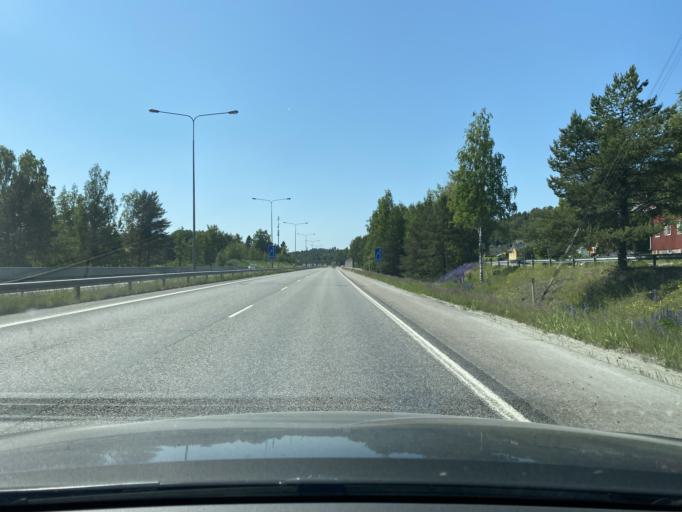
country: FI
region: Pirkanmaa
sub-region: Tampere
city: Nokia
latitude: 61.4836
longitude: 23.5656
